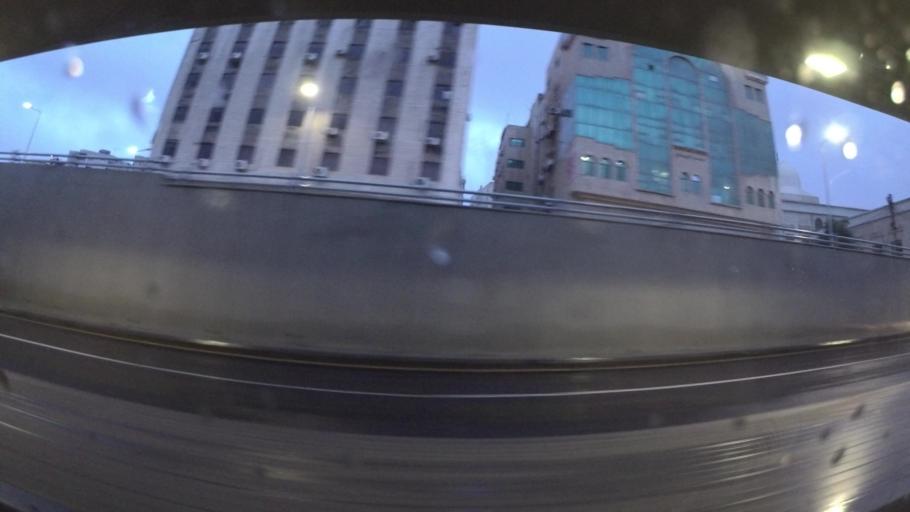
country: JO
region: Amman
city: Al Jubayhah
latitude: 31.9961
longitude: 35.8886
